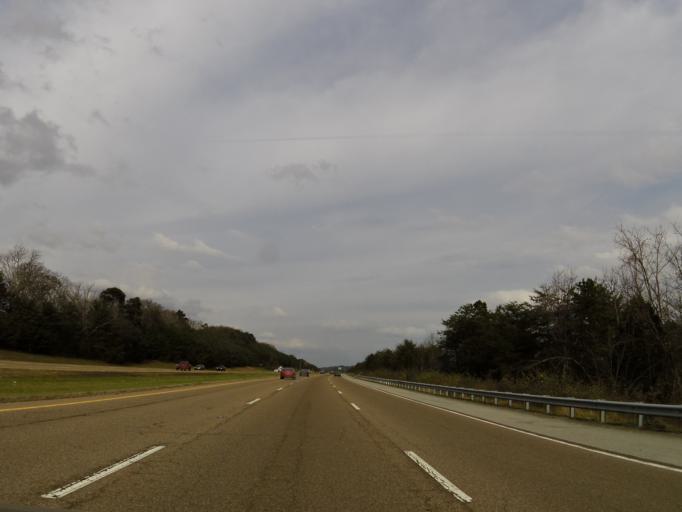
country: US
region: Tennessee
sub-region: Hamilton County
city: Red Bank
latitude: 35.1072
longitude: -85.3111
